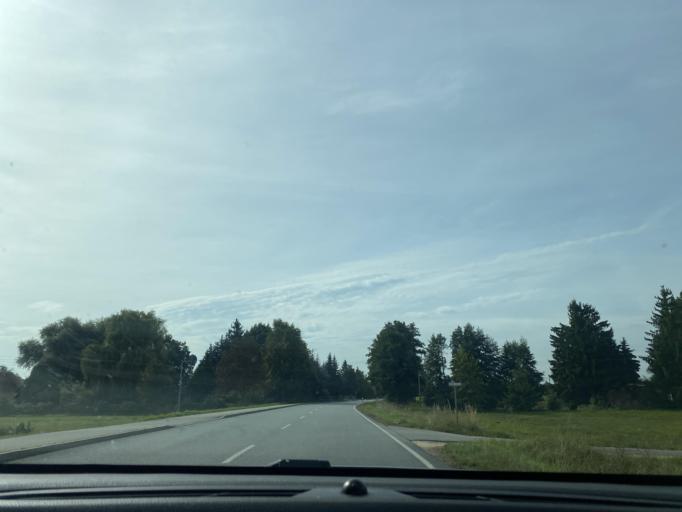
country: DE
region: Saxony
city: Quitzdorf
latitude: 51.2164
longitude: 14.7708
